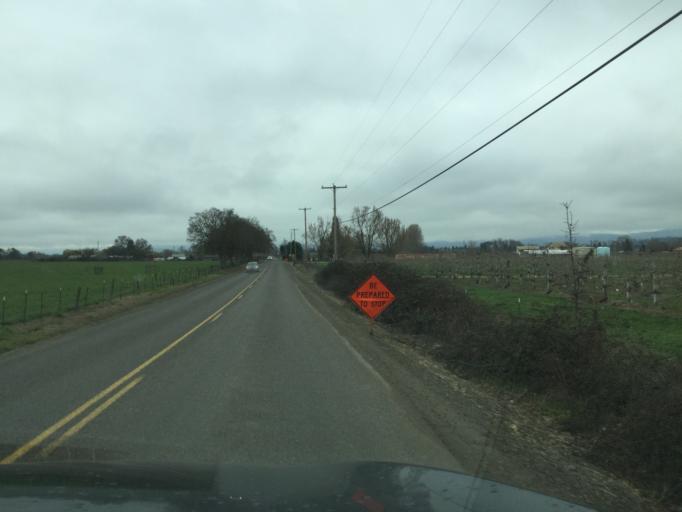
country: US
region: Oregon
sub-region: Jackson County
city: Central Point
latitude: 42.4002
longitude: -122.9093
